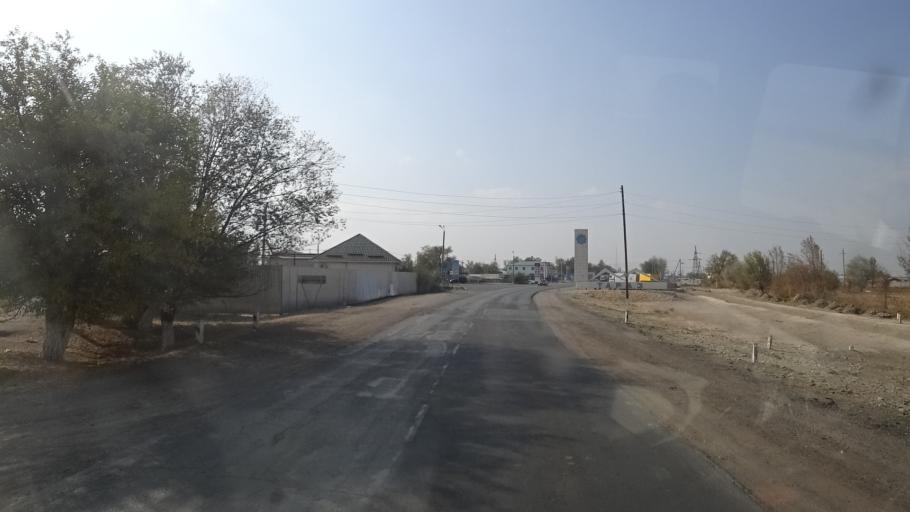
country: KZ
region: Zhambyl
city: Taraz
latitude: 42.9240
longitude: 71.4260
